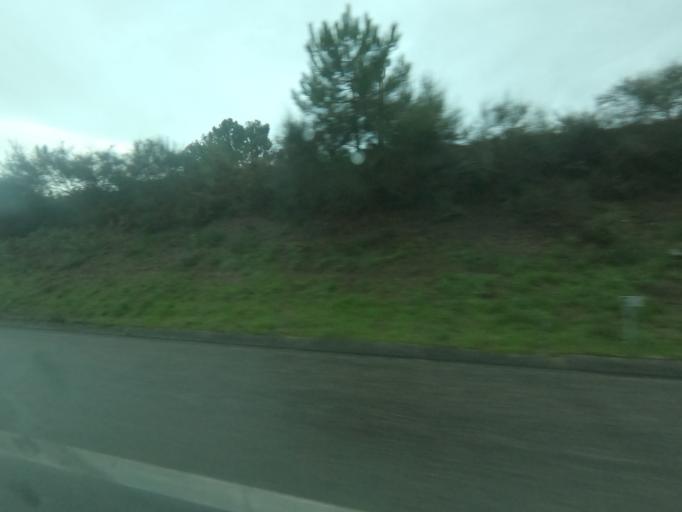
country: PT
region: Viana do Castelo
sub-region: Vila Nova de Cerveira
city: Vila Nova de Cerveira
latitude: 41.9471
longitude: -8.6671
